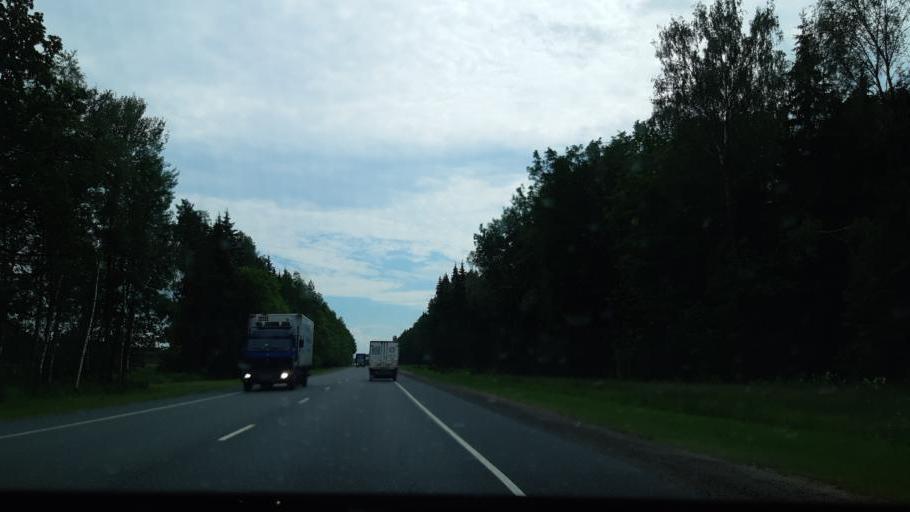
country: RU
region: Moskovskaya
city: Dorokhovo
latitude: 55.4423
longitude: 36.3518
